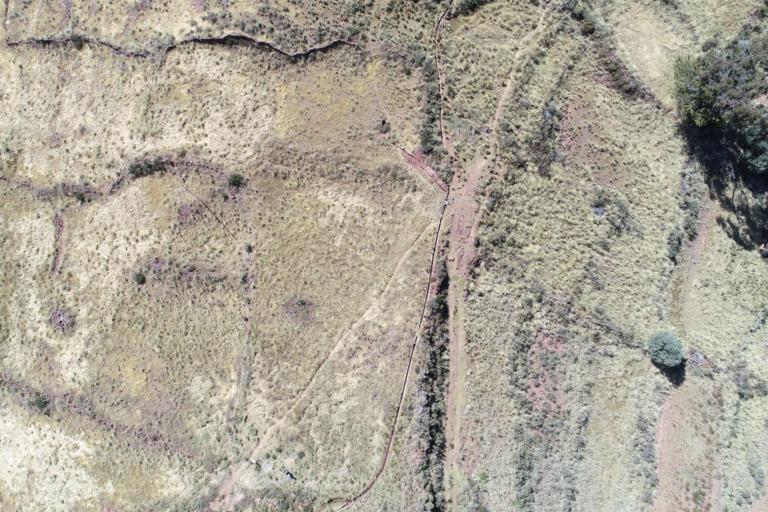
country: BO
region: La Paz
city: Tiahuanaco
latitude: -16.6096
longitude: -68.7666
